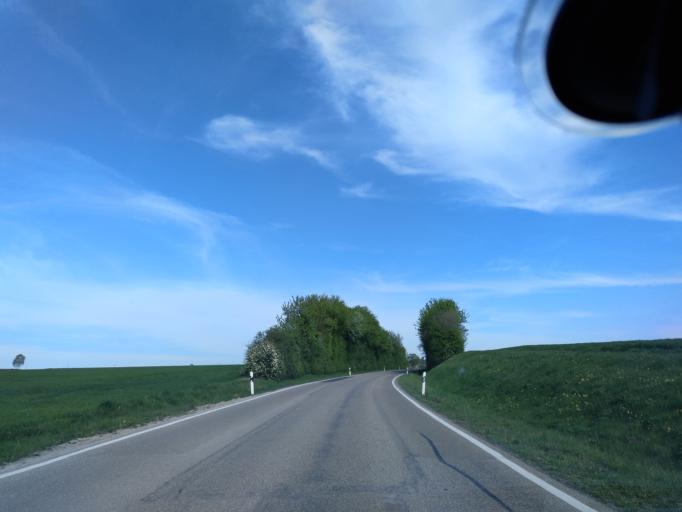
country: DE
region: Baden-Wuerttemberg
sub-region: Regierungsbezirk Stuttgart
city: Kupferzell
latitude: 49.2335
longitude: 9.7262
